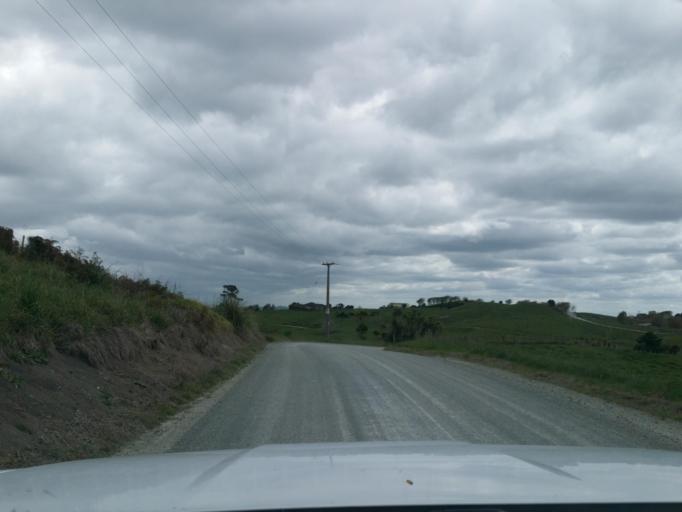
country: NZ
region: Auckland
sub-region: Auckland
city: Wellsford
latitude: -36.2479
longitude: 174.3652
